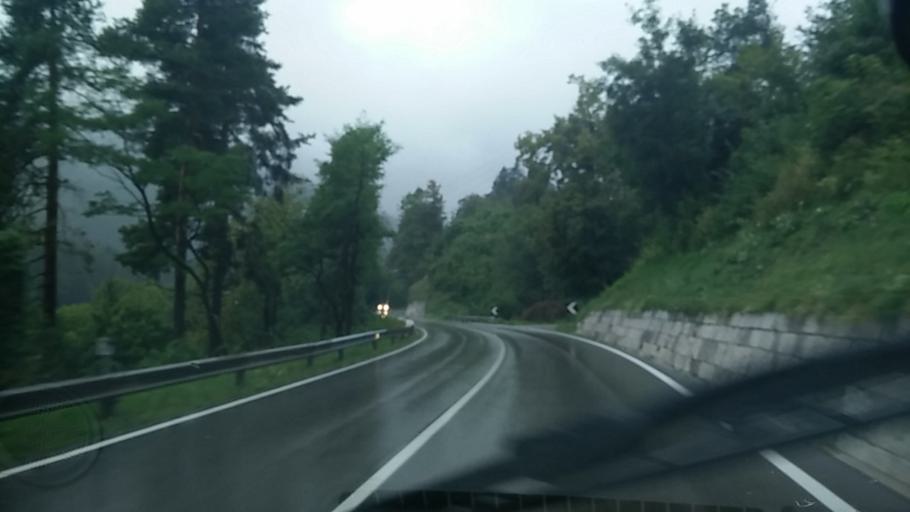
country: IT
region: Friuli Venezia Giulia
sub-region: Provincia di Udine
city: Tarvisio
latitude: 46.5058
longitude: 13.5903
